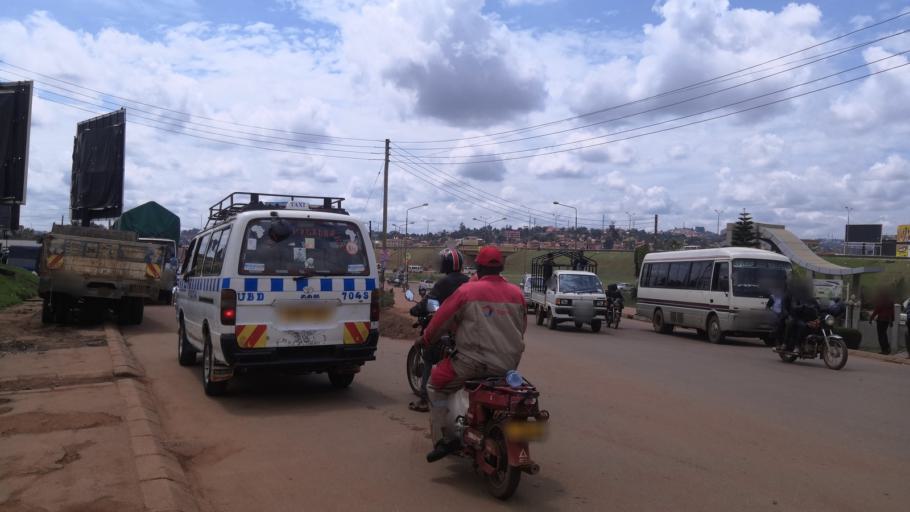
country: UG
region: Central Region
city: Kampala Central Division
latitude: 0.3482
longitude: 32.5641
